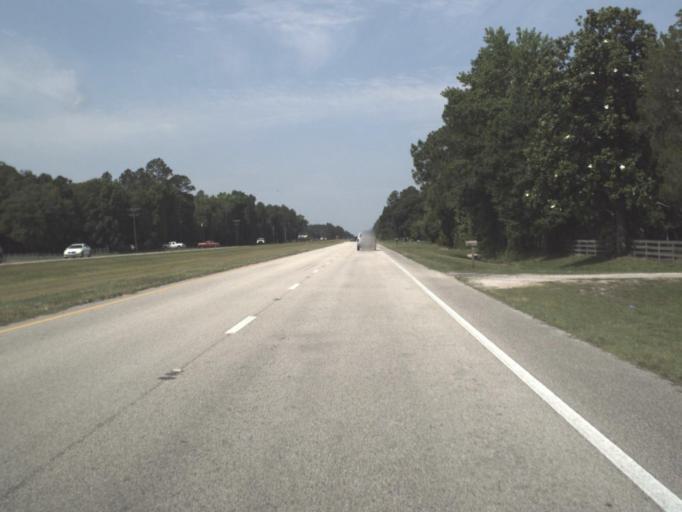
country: US
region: Florida
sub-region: Alachua County
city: Waldo
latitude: 29.7803
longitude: -82.1807
